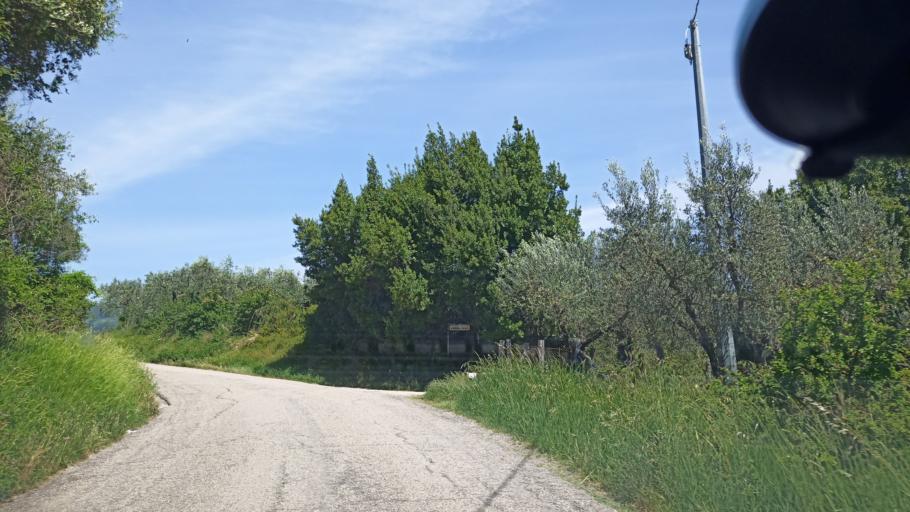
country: IT
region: Latium
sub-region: Provincia di Rieti
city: Torri in Sabina
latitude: 42.3557
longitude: 12.6346
